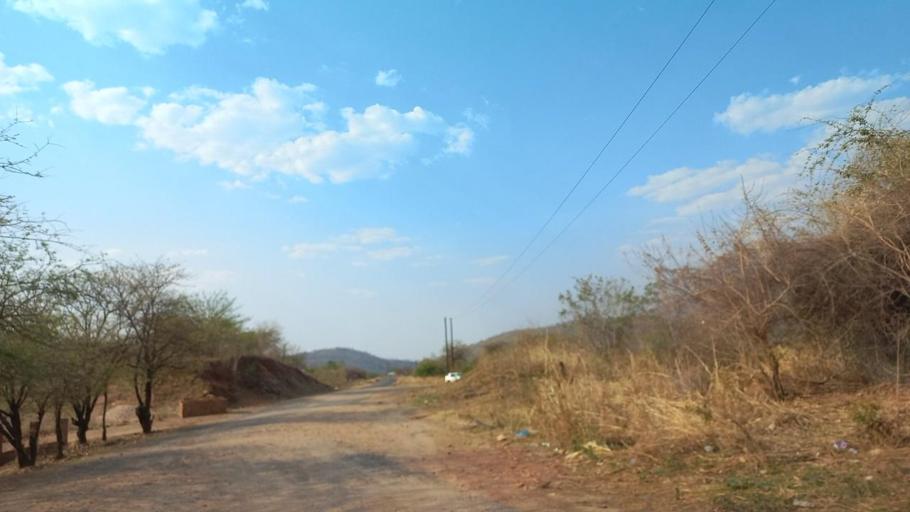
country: ZM
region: Lusaka
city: Luangwa
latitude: -14.9955
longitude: 30.2137
